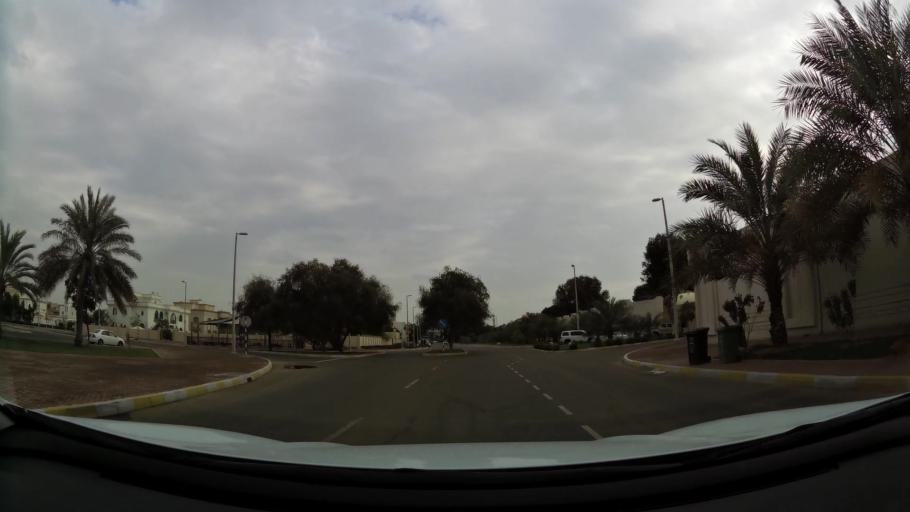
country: AE
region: Abu Dhabi
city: Abu Dhabi
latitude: 24.4383
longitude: 54.3968
